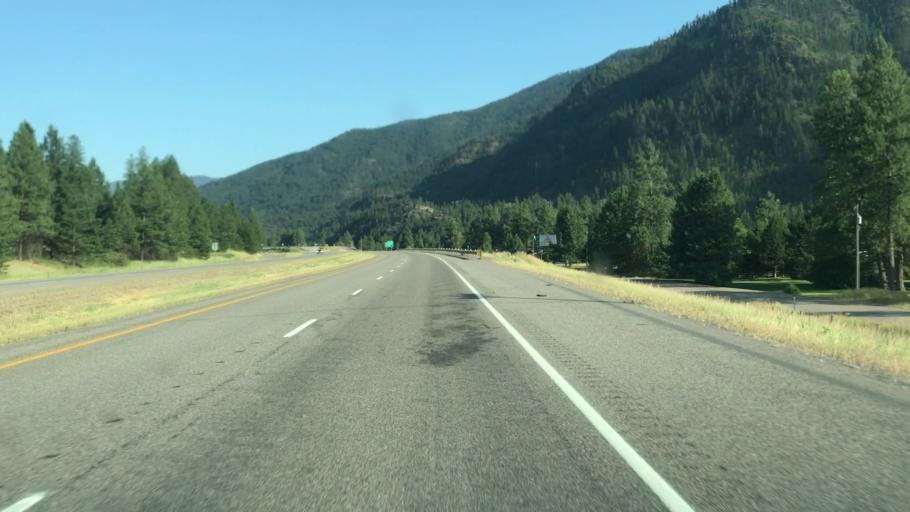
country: US
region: Montana
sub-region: Missoula County
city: Frenchtown
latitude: 47.0115
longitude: -114.5017
